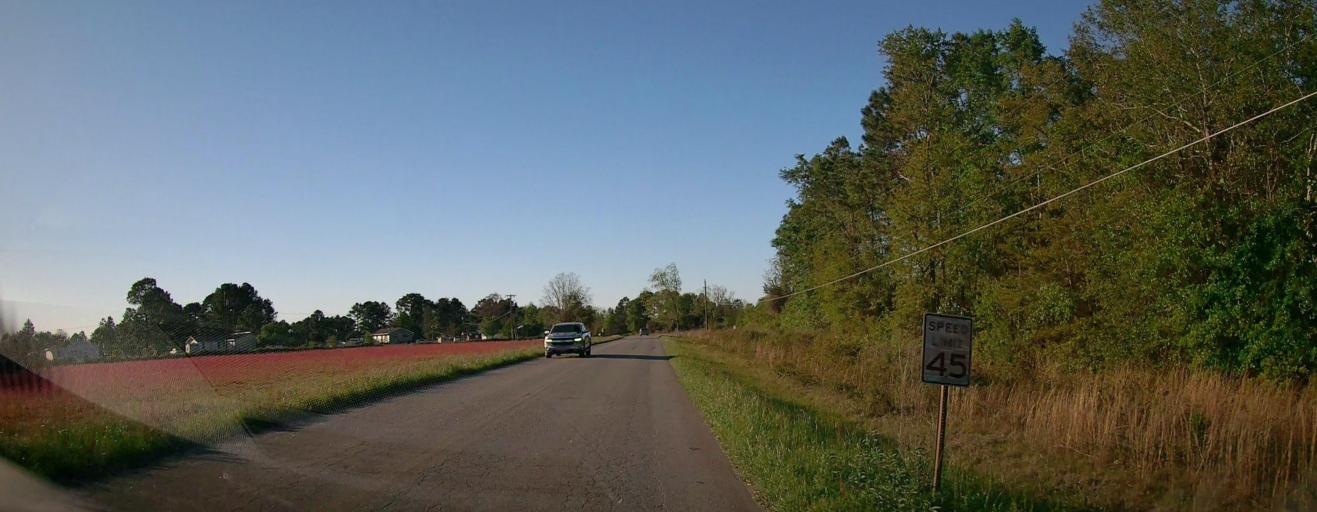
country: US
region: Georgia
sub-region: Ben Hill County
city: Fitzgerald
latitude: 31.6978
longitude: -83.2218
